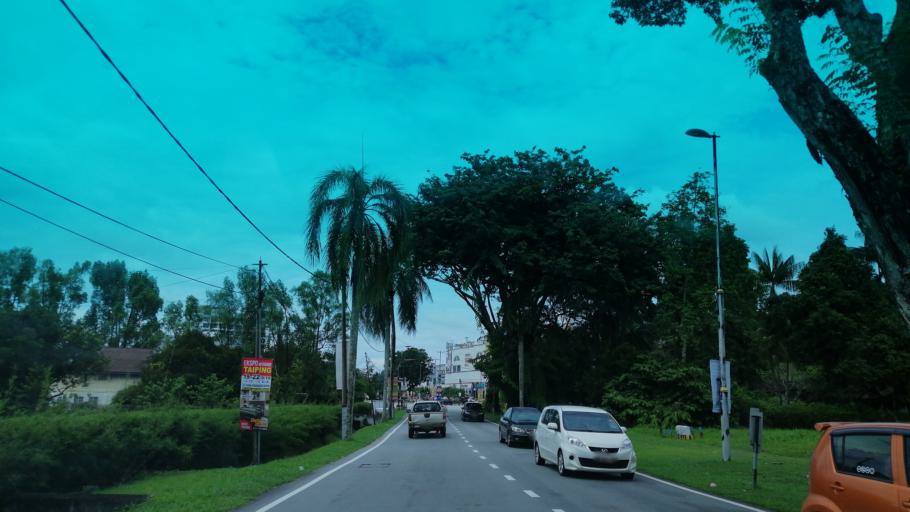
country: MY
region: Perak
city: Taiping
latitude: 4.8639
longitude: 100.7329
